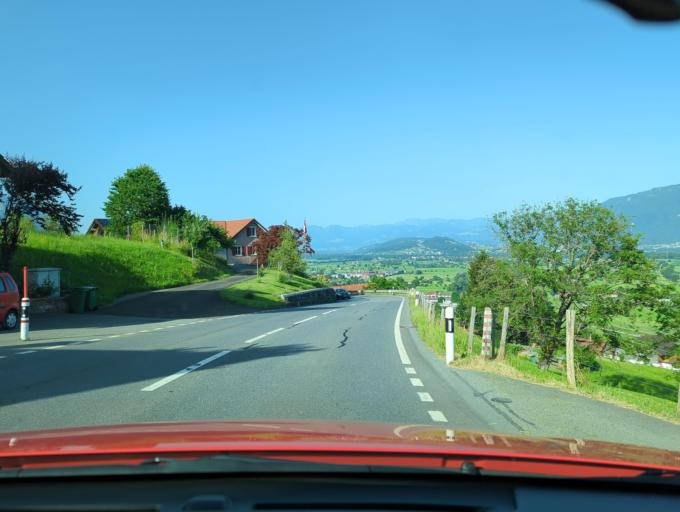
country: CH
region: Saint Gallen
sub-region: Wahlkreis Werdenberg
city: Gams
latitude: 47.1952
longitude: 9.4312
